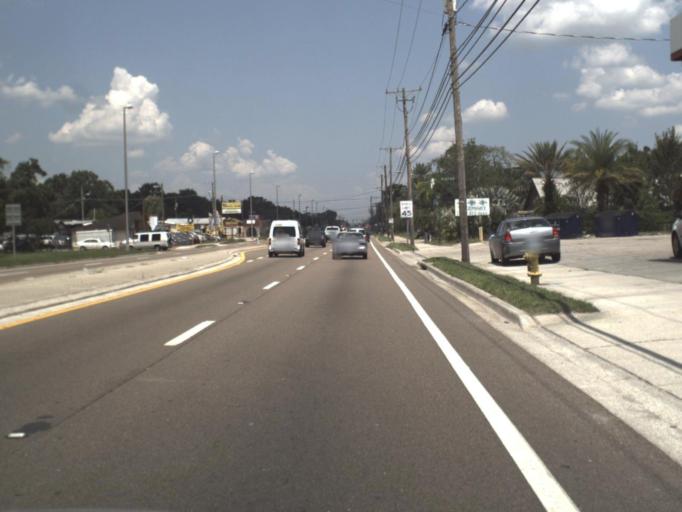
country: US
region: Florida
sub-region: Hillsborough County
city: University
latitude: 28.0604
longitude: -82.4511
